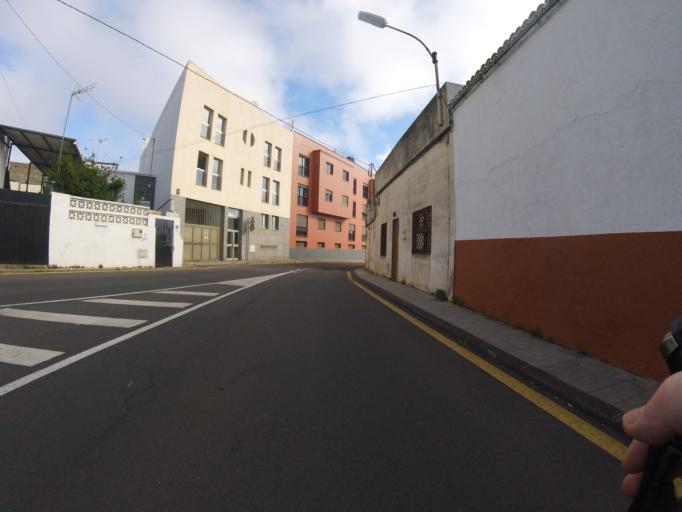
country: ES
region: Canary Islands
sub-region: Provincia de Santa Cruz de Tenerife
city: La Laguna
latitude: 28.4835
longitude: -16.3229
